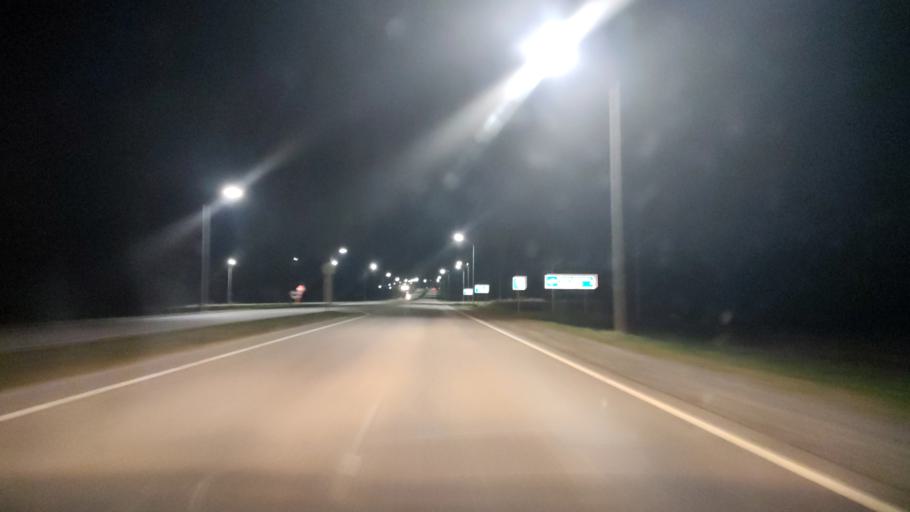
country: RU
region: Belgorod
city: Staryy Oskol
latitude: 51.3886
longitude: 37.8638
